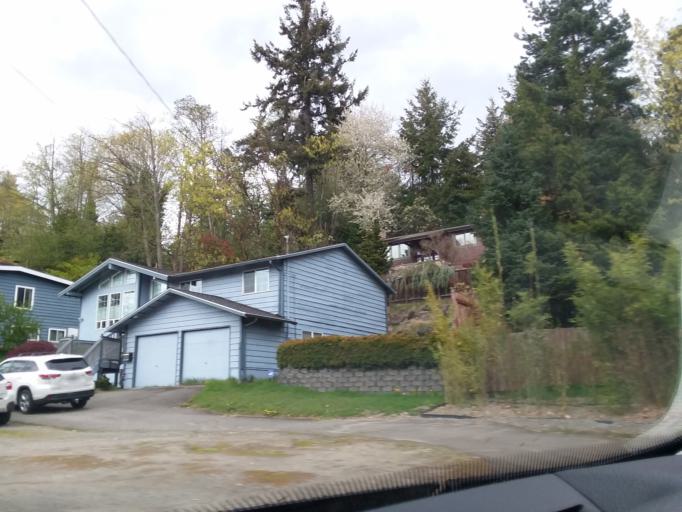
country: US
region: Washington
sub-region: King County
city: Lake Forest Park
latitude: 47.6898
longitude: -122.3015
